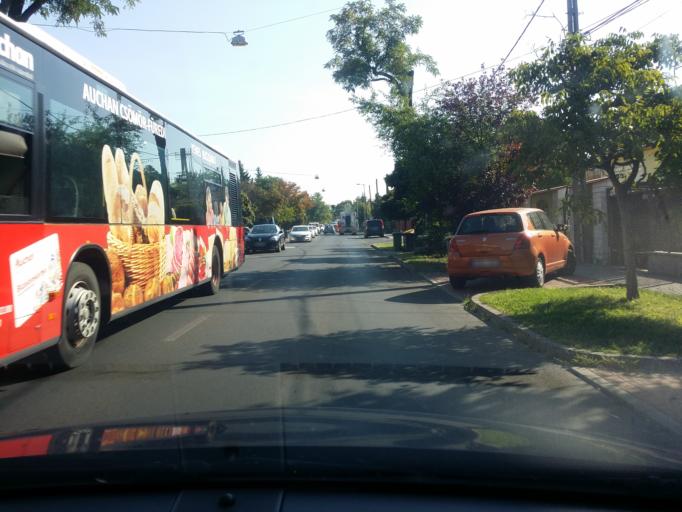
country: HU
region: Budapest
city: Budapest XVI. keruelet
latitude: 47.5255
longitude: 19.1608
